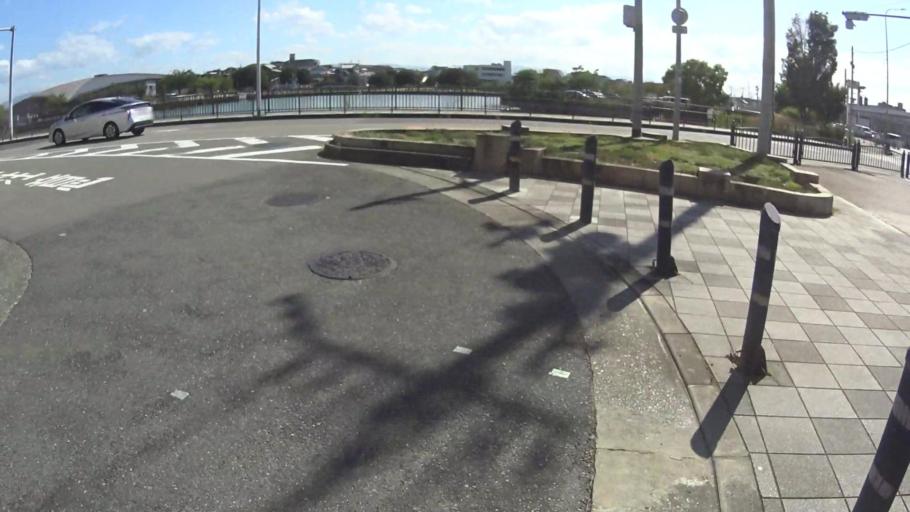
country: JP
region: Ehime
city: Kihoku-cho
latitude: 33.3826
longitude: 132.8256
